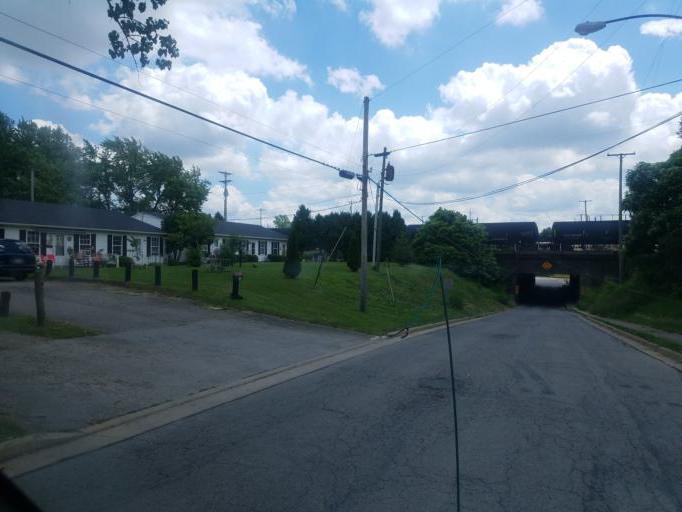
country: US
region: Ohio
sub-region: Huron County
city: Willard
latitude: 41.0633
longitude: -82.7332
